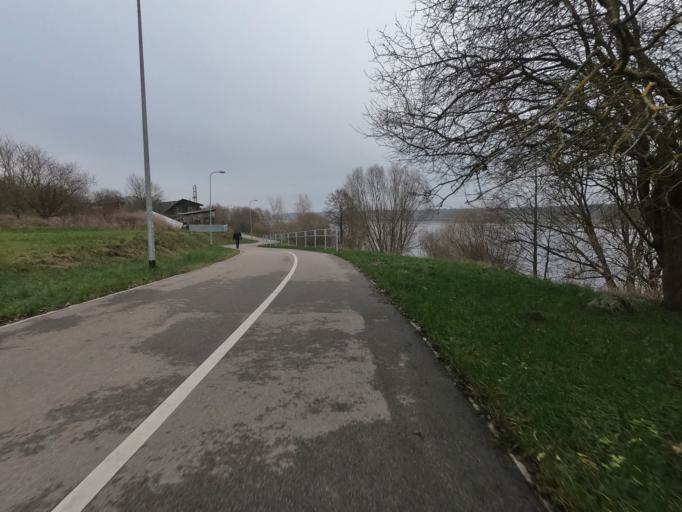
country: LV
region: Kekava
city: Kekava
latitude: 56.8801
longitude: 24.2192
